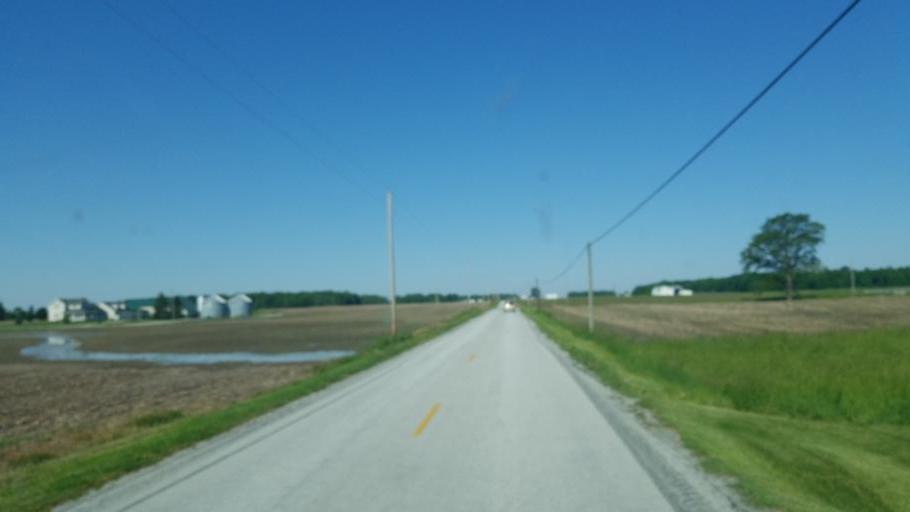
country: US
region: Ohio
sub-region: Hardin County
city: Kenton
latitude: 40.6438
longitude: -83.6539
